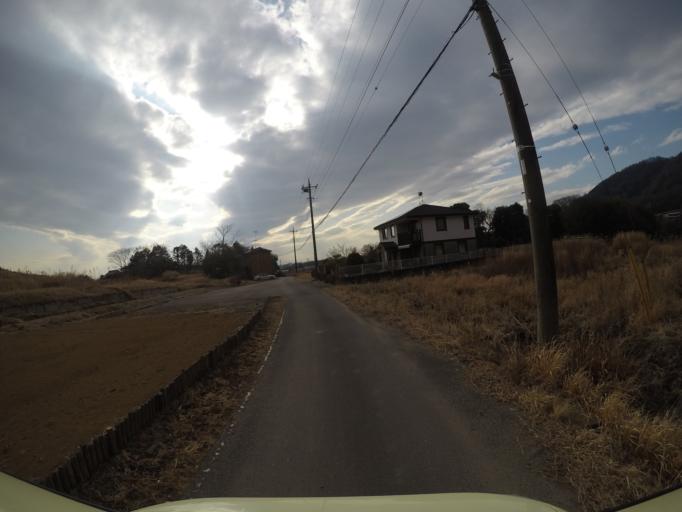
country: JP
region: Ibaraki
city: Tsukuba
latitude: 36.1795
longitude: 140.1163
